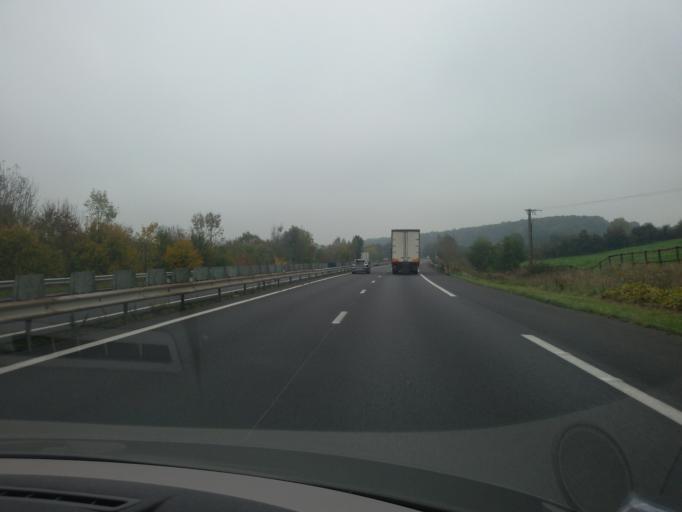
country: FR
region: Lower Normandy
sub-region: Departement du Calvados
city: Dozule
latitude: 49.2488
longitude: 0.0275
